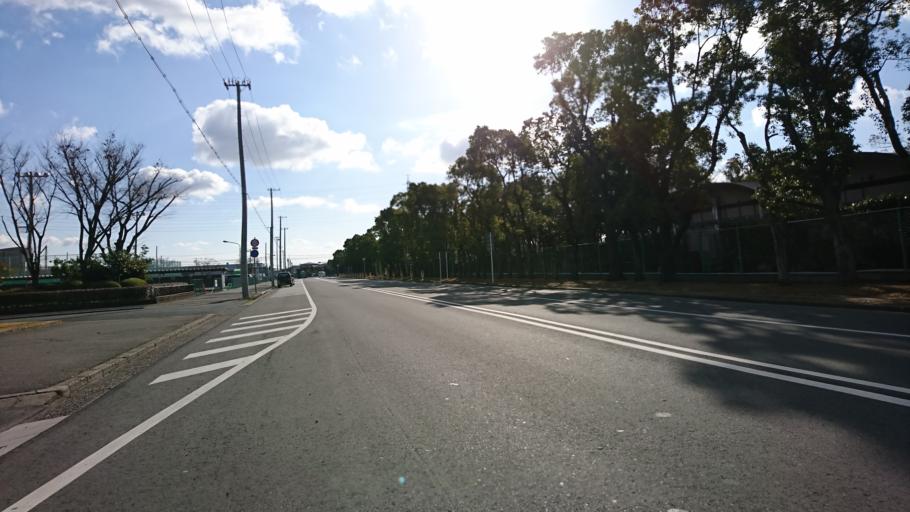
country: JP
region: Hyogo
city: Kakogawacho-honmachi
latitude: 34.7544
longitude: 134.7910
